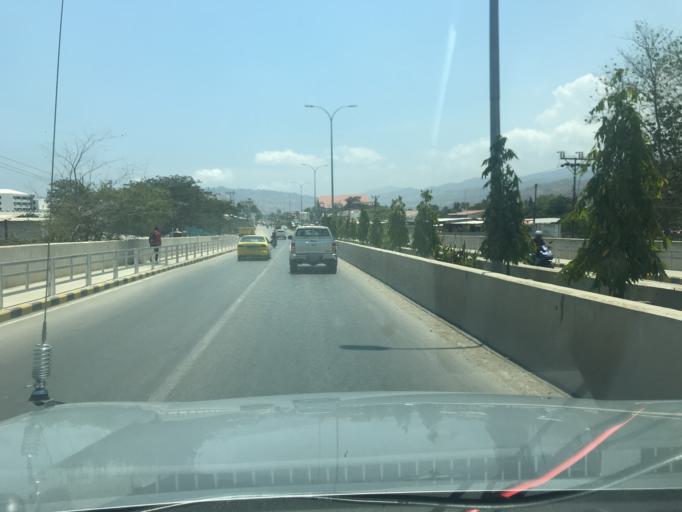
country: TL
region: Dili
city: Dili
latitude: -8.5542
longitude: 125.5376
